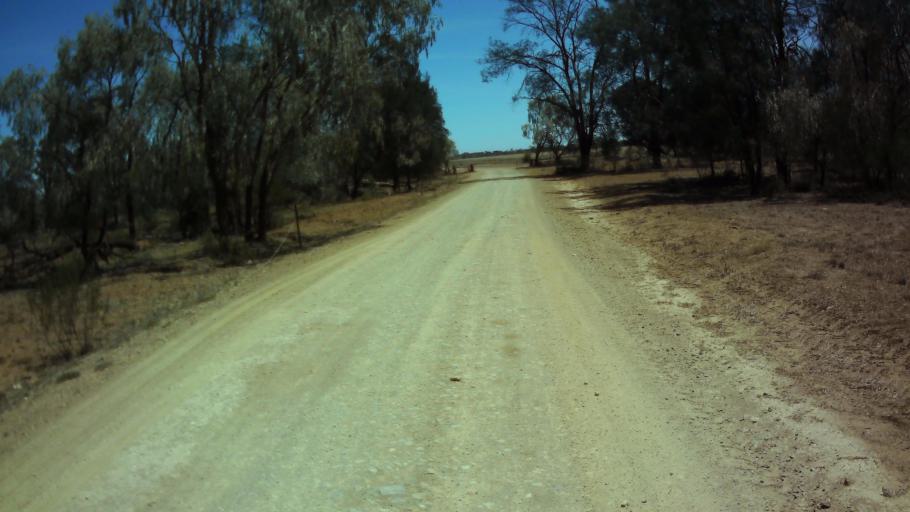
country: AU
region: New South Wales
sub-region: Bland
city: West Wyalong
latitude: -33.8178
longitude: 147.6481
